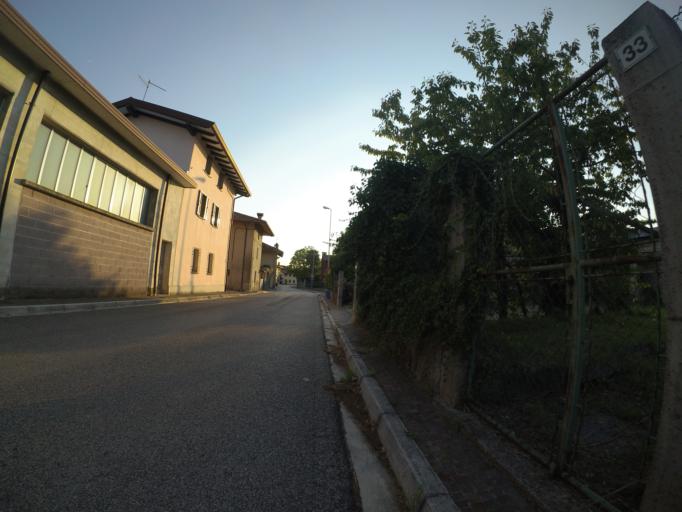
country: IT
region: Friuli Venezia Giulia
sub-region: Provincia di Udine
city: Campoformido
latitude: 46.0177
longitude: 13.1604
